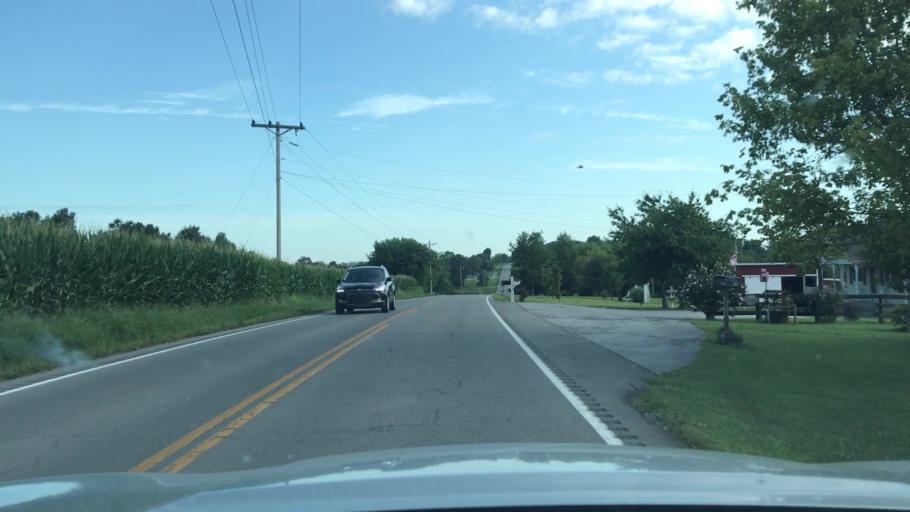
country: US
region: Kentucky
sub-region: Todd County
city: Elkton
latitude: 36.8767
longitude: -87.1668
